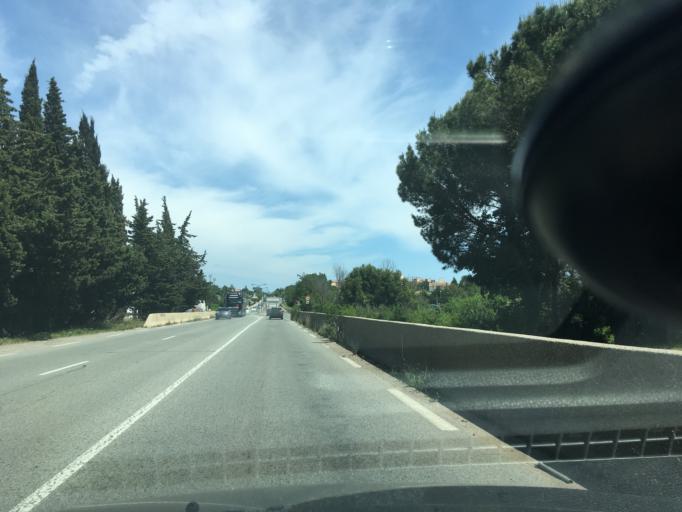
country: FR
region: Provence-Alpes-Cote d'Azur
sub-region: Departement du Var
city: Puget-sur-Argens
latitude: 43.4582
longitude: 6.6765
